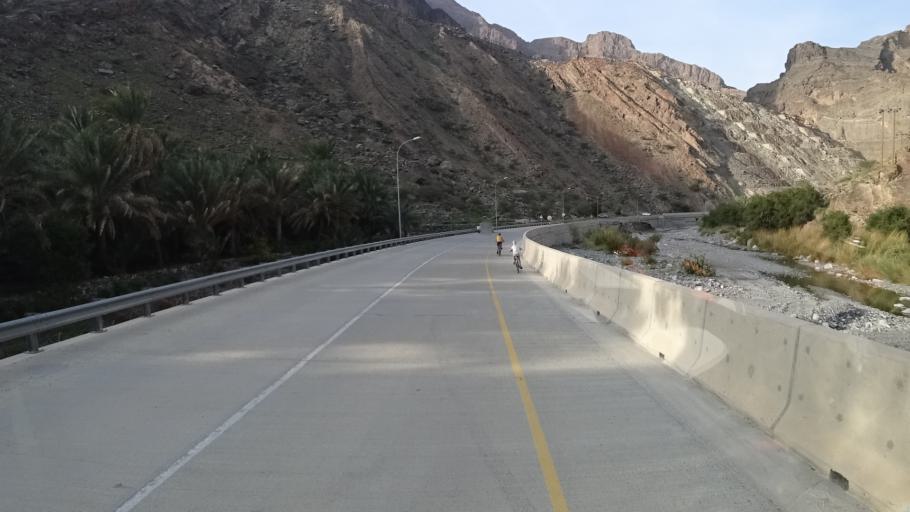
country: OM
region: Al Batinah
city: Bayt al `Awabi
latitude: 23.2843
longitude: 57.4654
